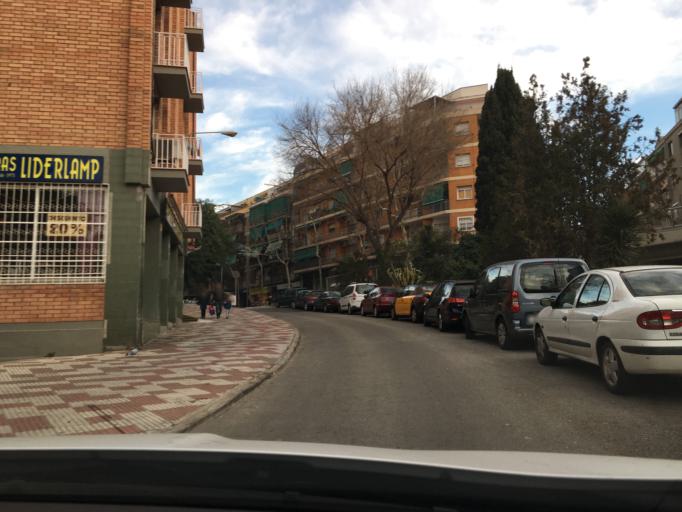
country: ES
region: Catalonia
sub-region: Provincia de Barcelona
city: Santa Coloma de Gramenet
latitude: 41.4461
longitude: 2.2105
